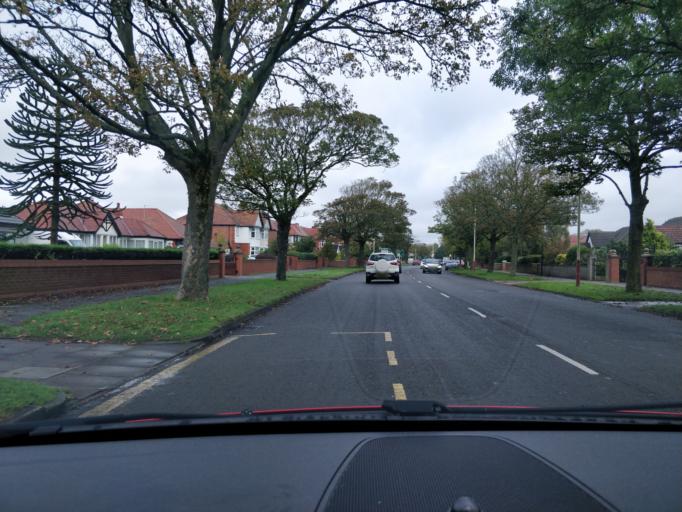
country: GB
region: England
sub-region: Sefton
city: Southport
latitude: 53.6107
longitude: -3.0223
